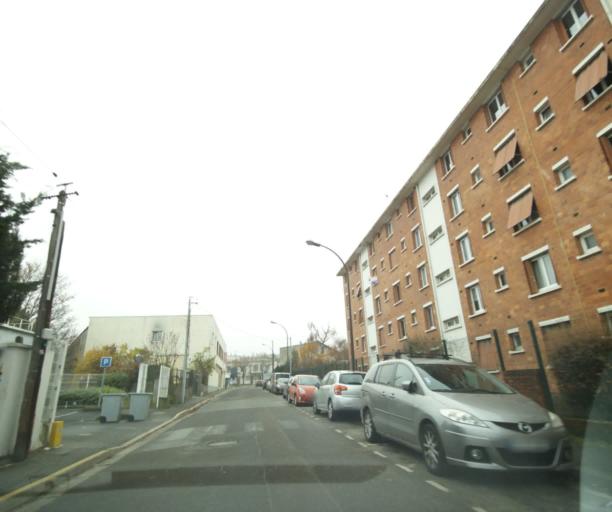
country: FR
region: Ile-de-France
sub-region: Departement de Seine-Saint-Denis
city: Livry-Gargan
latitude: 48.9255
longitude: 2.5468
